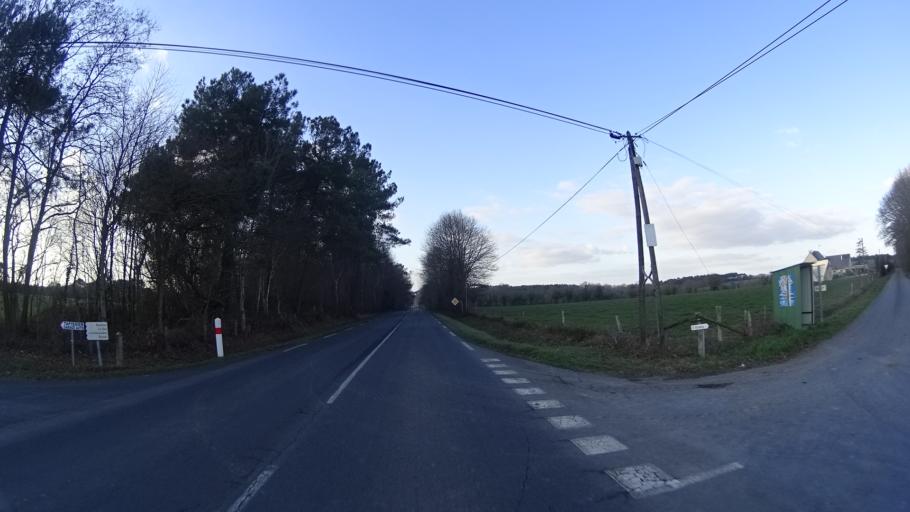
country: FR
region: Pays de la Loire
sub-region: Departement de la Loire-Atlantique
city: Fegreac
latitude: 47.5757
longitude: -1.9838
